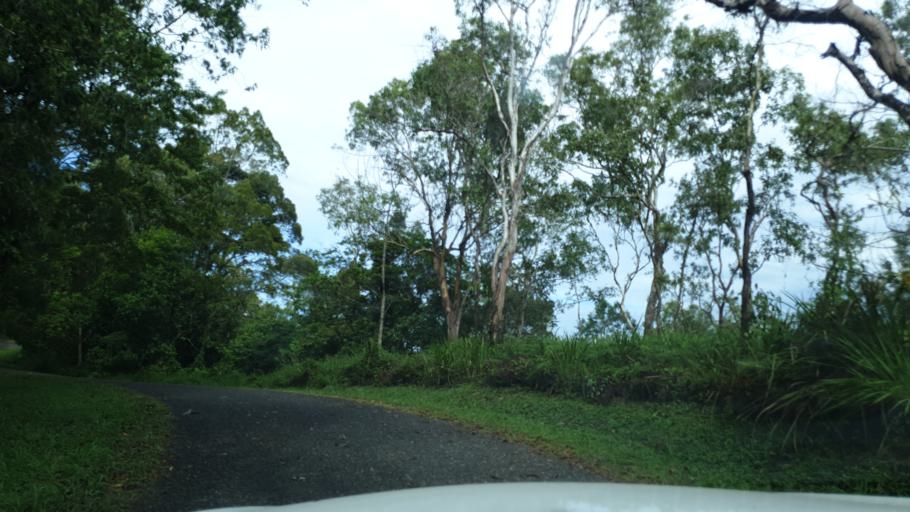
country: PG
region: National Capital
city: Port Moresby
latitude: -9.4327
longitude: 147.3715
